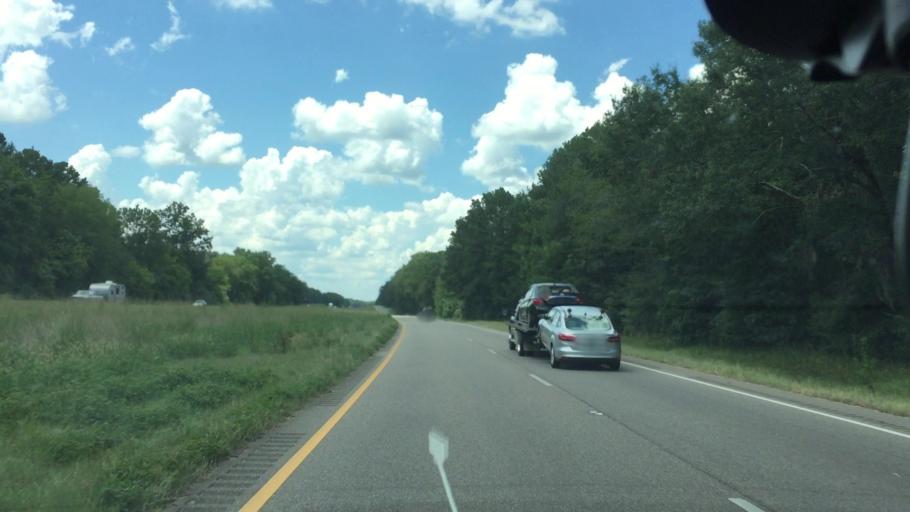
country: US
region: Alabama
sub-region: Montgomery County
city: Pike Road
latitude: 32.1358
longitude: -86.0892
